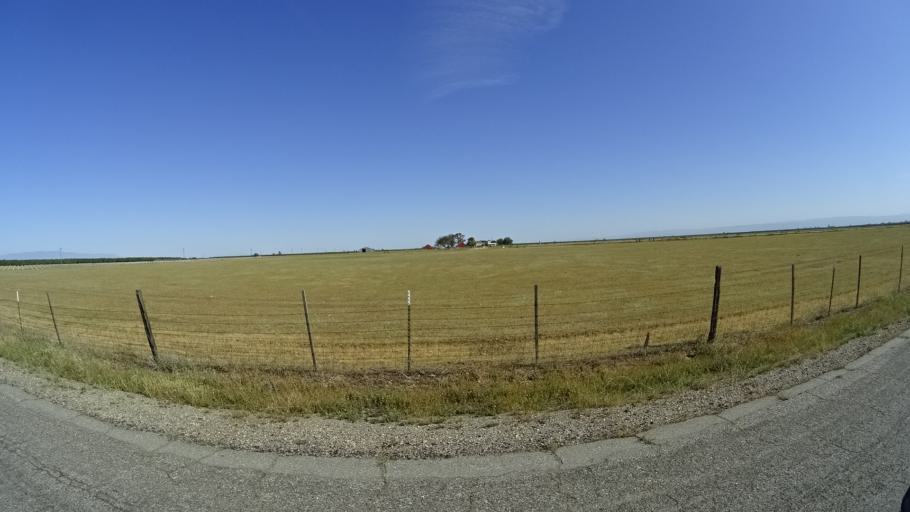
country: US
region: California
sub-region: Glenn County
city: Willows
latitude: 39.6112
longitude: -122.1542
